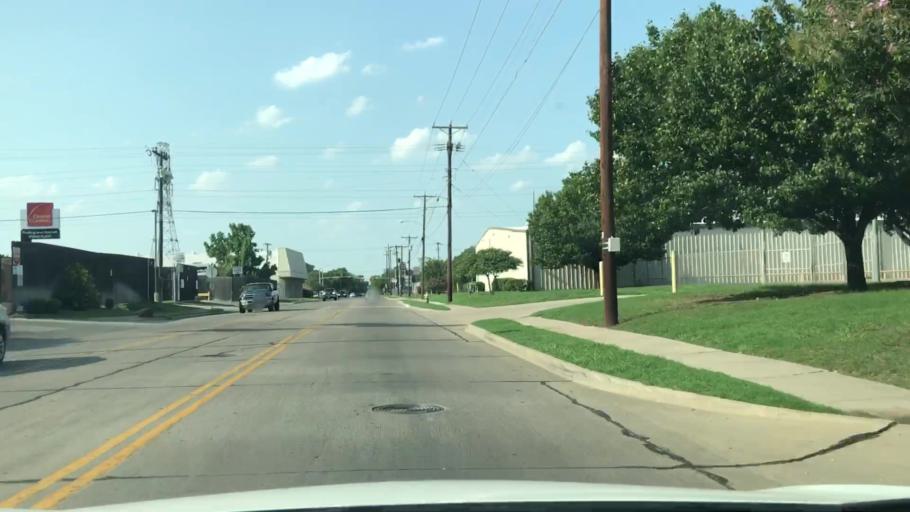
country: US
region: Texas
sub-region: Dallas County
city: Irving
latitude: 32.8151
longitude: -96.9343
